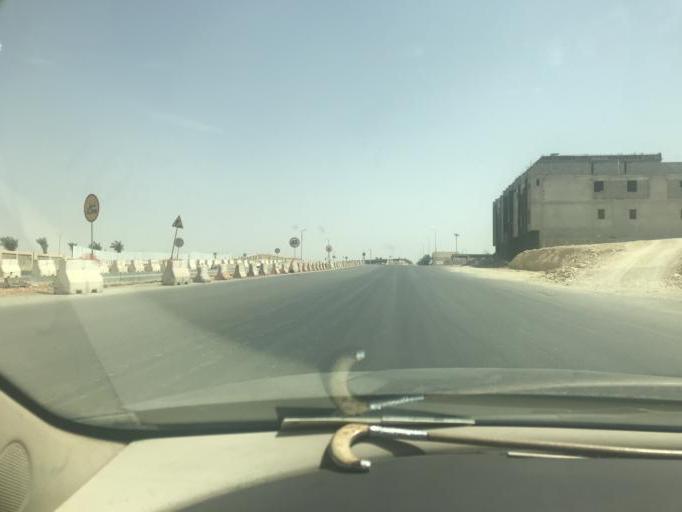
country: SA
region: Ar Riyad
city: Riyadh
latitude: 24.8329
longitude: 46.6924
